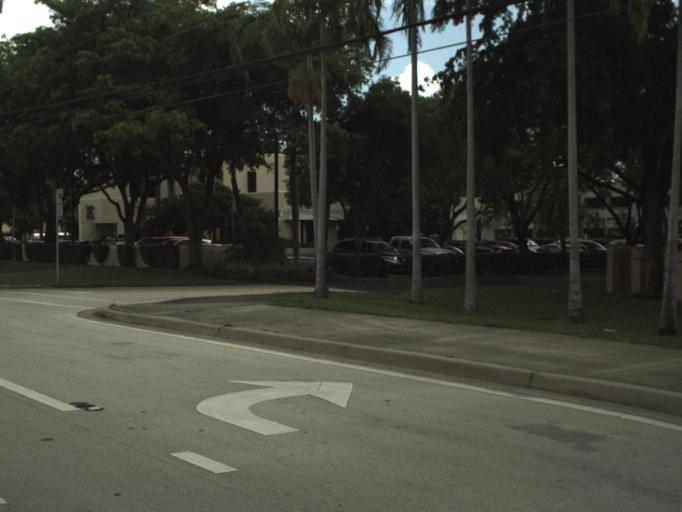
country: US
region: Florida
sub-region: Broward County
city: Lauderdale Lakes
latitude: 26.1828
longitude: -80.2035
